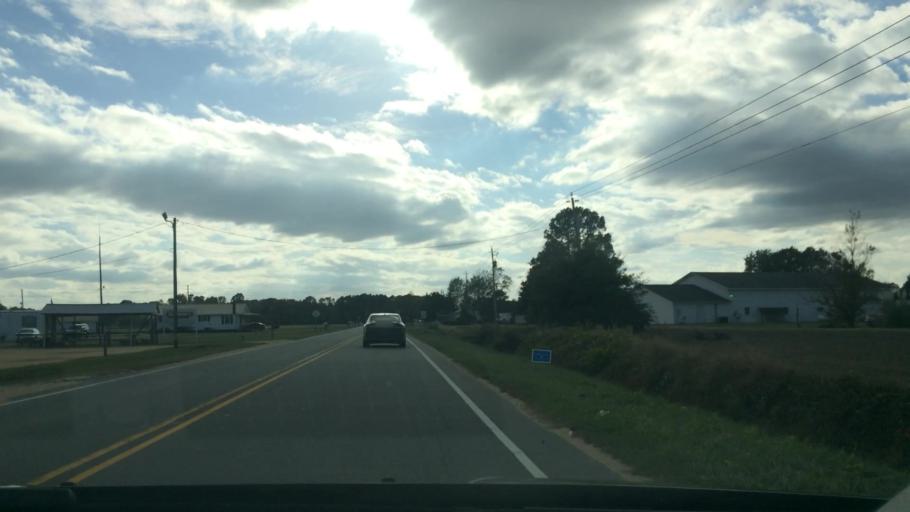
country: US
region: North Carolina
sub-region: Wayne County
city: Elroy
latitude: 35.4018
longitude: -77.9005
